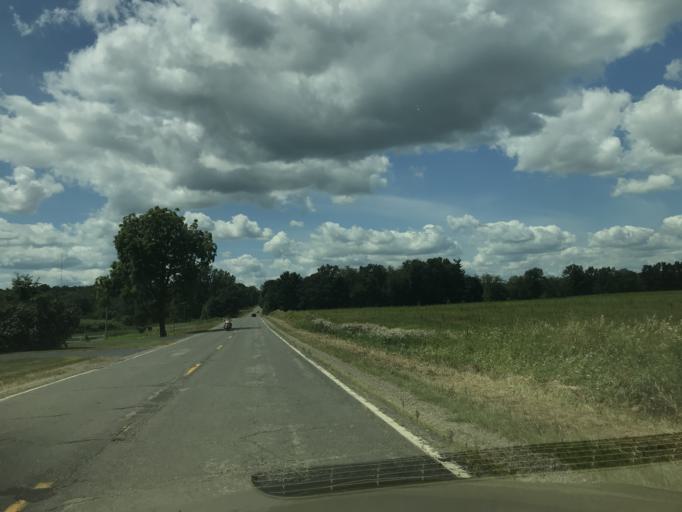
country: US
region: Michigan
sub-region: Ingham County
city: Leslie
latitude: 42.4509
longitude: -84.5376
